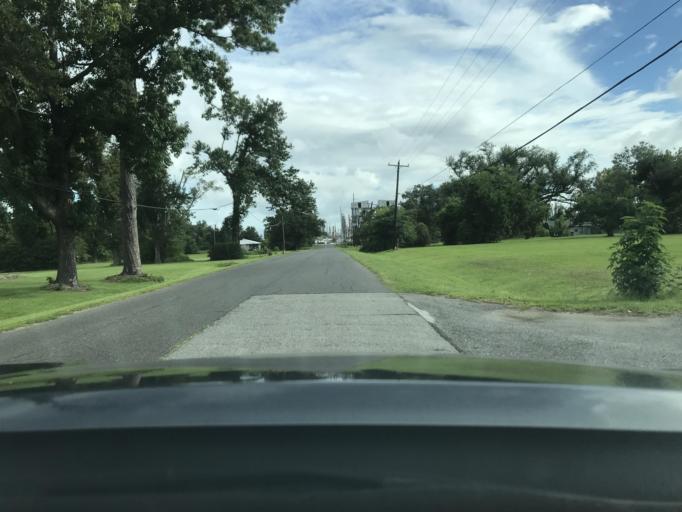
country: US
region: Louisiana
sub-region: Calcasieu Parish
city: Westlake
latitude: 30.2575
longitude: -93.2751
